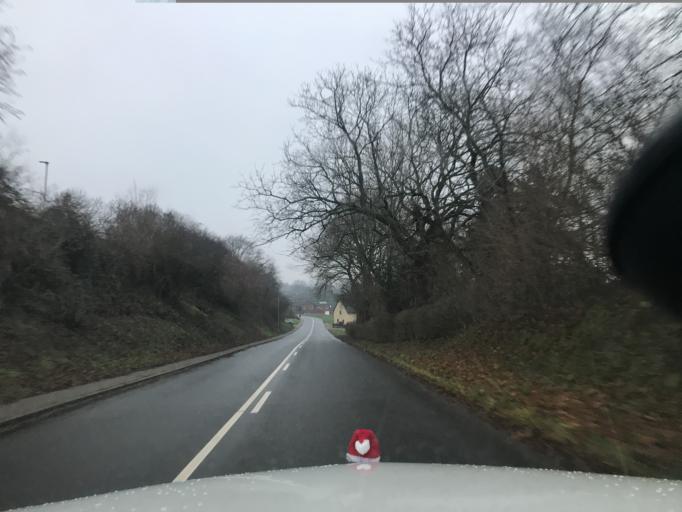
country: DK
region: South Denmark
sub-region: Sonderborg Kommune
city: Grasten
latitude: 54.8917
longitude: 9.5623
